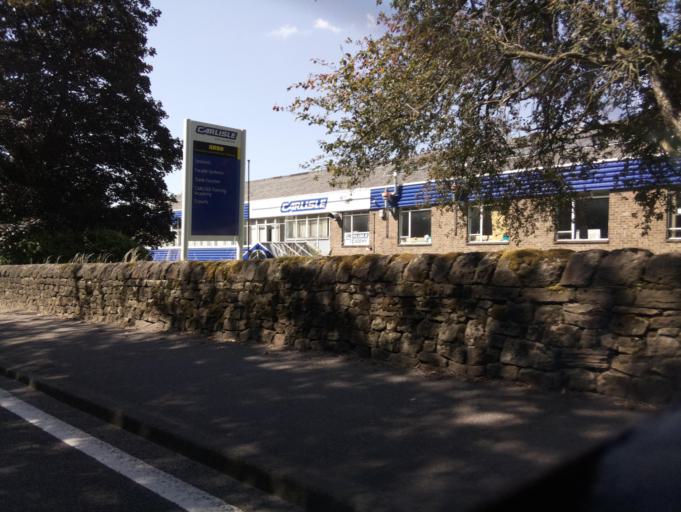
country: GB
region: England
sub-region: Derbyshire
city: Belper
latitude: 53.0110
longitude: -1.4811
